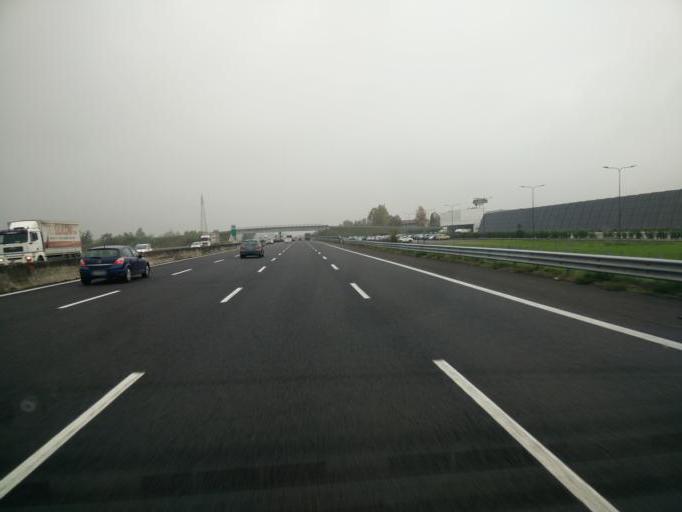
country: IT
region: Emilia-Romagna
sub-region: Provincia di Modena
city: San Damaso
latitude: 44.5897
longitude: 10.9526
